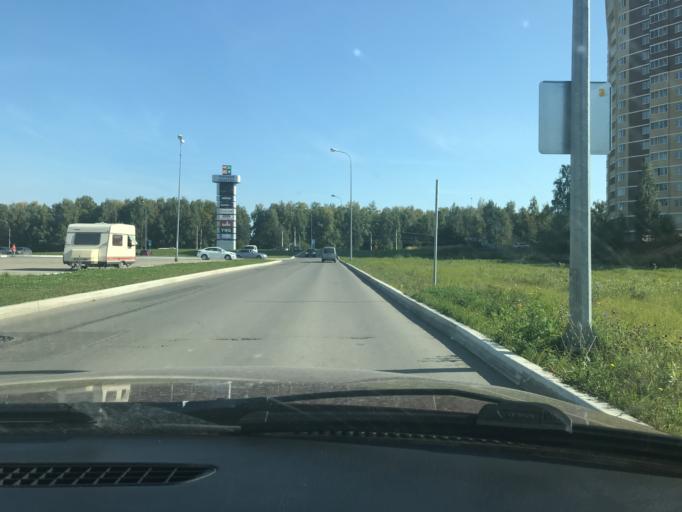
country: RU
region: Kaluga
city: Kaluga
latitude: 54.5852
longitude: 36.2495
